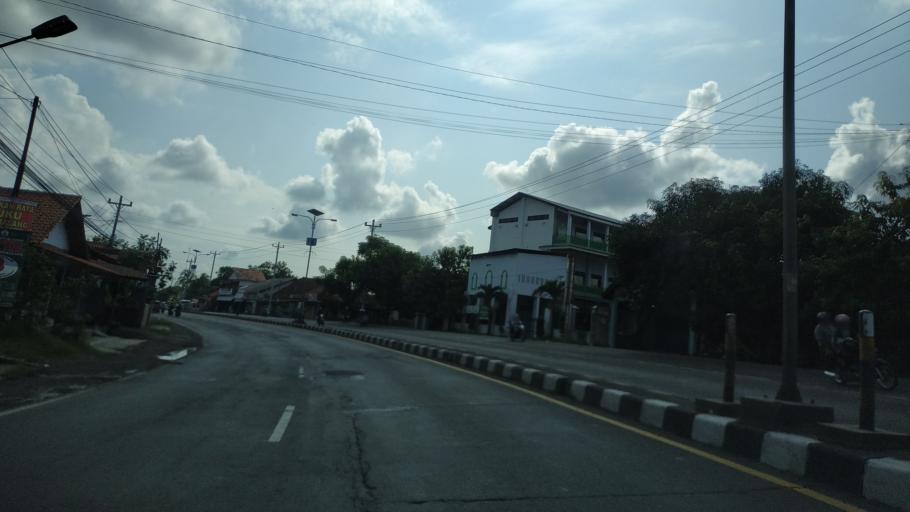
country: ID
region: Central Java
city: Comal
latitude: -6.8975
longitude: 109.5406
